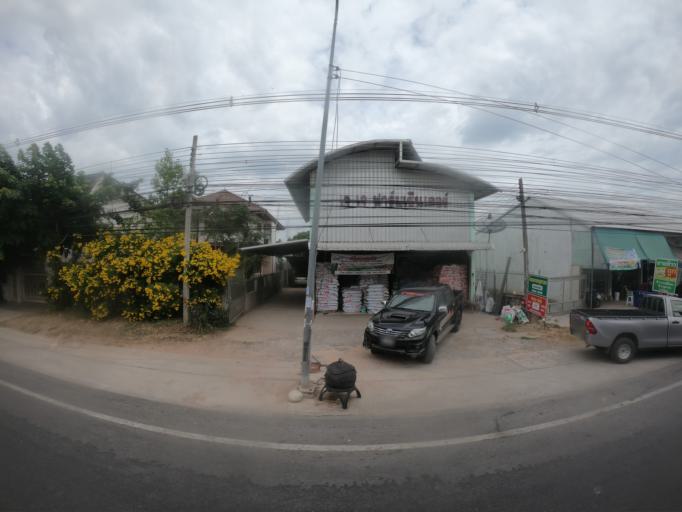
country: TH
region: Maha Sarakham
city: Maha Sarakham
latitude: 16.1702
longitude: 103.3227
